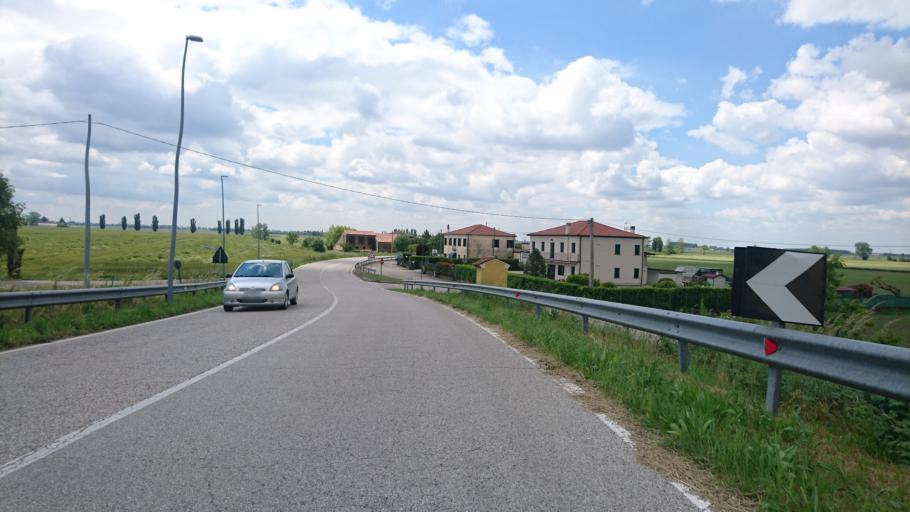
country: IT
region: Veneto
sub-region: Provincia di Padova
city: Vighizzolo d'Este
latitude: 45.1411
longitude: 11.6329
